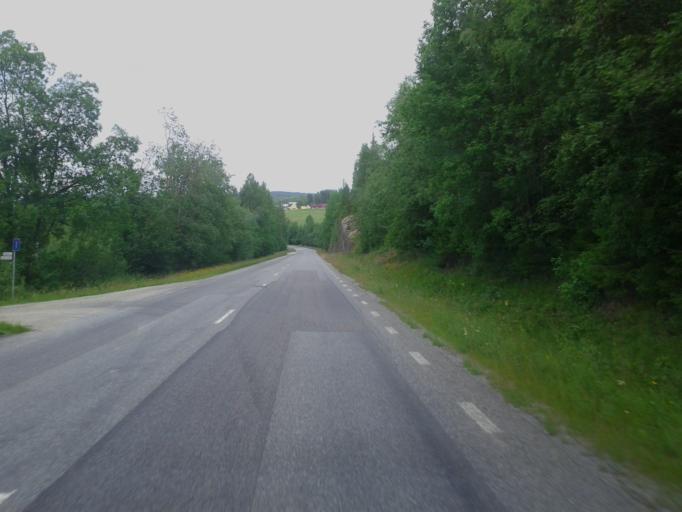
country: SE
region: Vaesternorrland
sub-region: OErnskoeldsviks Kommun
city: Bjasta
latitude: 63.2398
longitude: 18.4395
